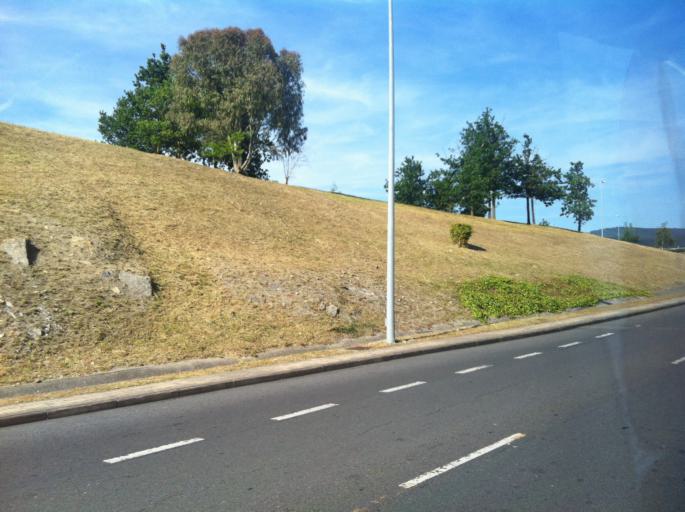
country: ES
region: Basque Country
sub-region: Bizkaia
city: Sondika
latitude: 43.3061
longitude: -2.9039
